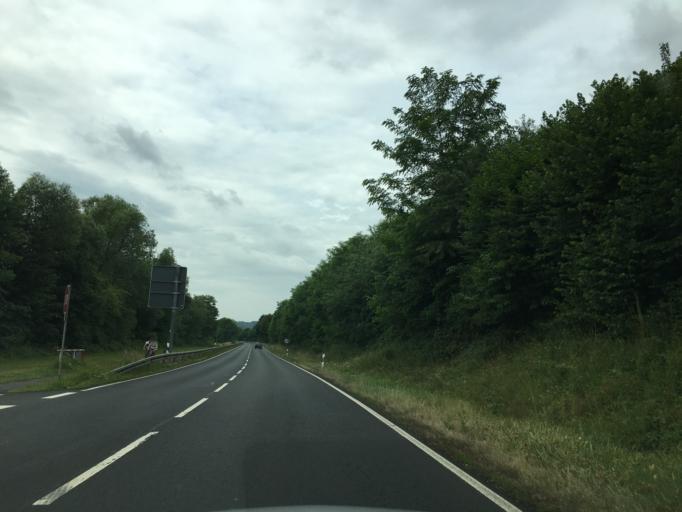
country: DE
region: Hesse
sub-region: Regierungsbezirk Darmstadt
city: Wachtersbach
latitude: 50.2641
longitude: 9.3071
